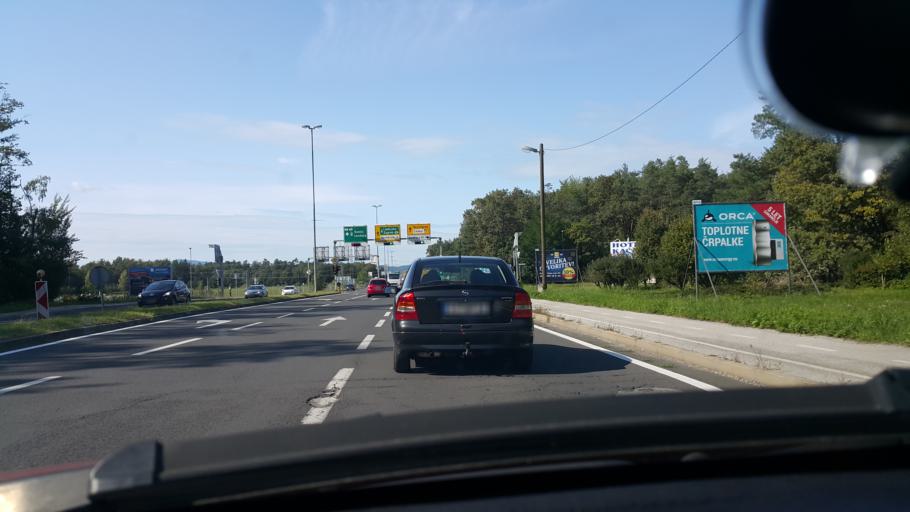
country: SI
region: Miklavz na Dravskem Polju
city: Miklavz na Dravskem Polju
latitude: 46.5171
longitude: 15.6852
